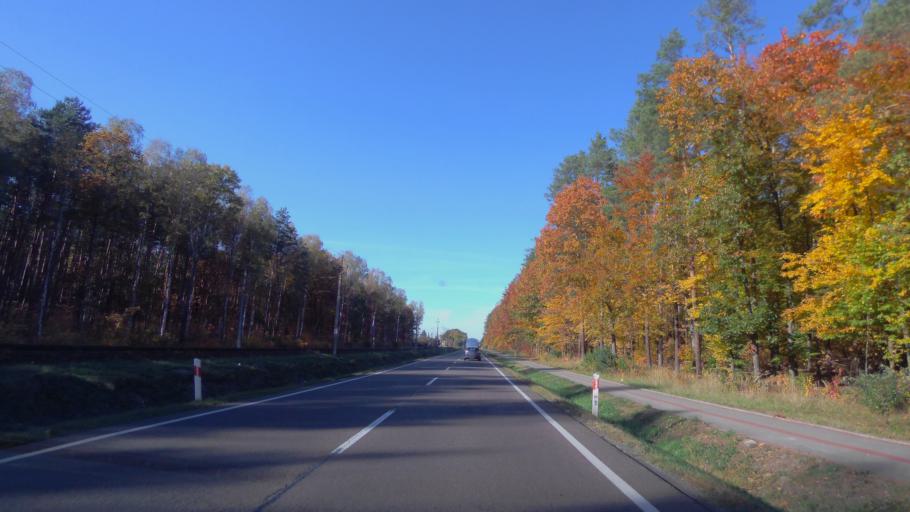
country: PL
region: Subcarpathian Voivodeship
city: Nowa Sarzyna
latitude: 50.3126
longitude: 22.3572
